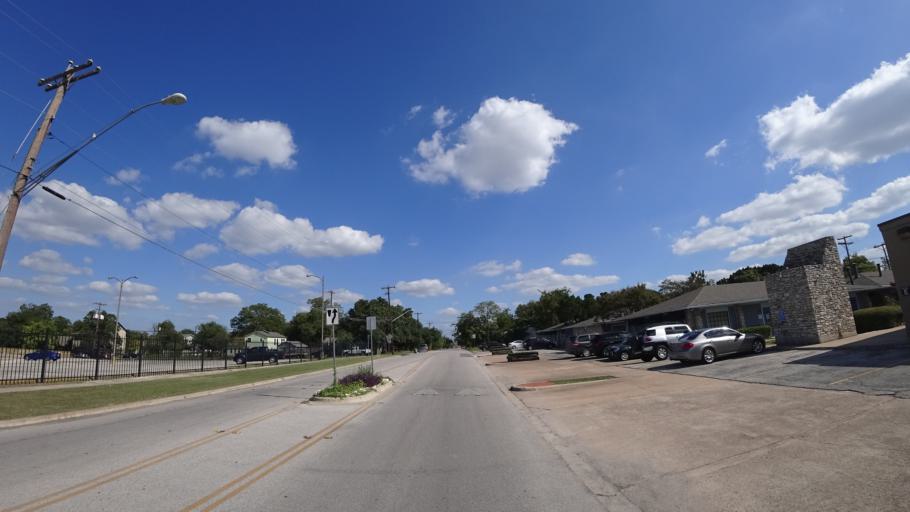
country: US
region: Texas
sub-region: Travis County
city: Austin
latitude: 30.3146
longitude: -97.7138
